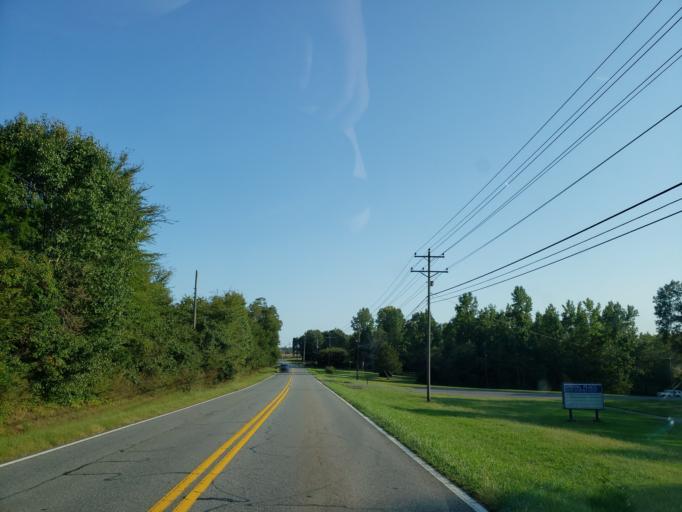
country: US
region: Georgia
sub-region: Murray County
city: Chatsworth
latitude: 34.7729
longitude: -84.8240
